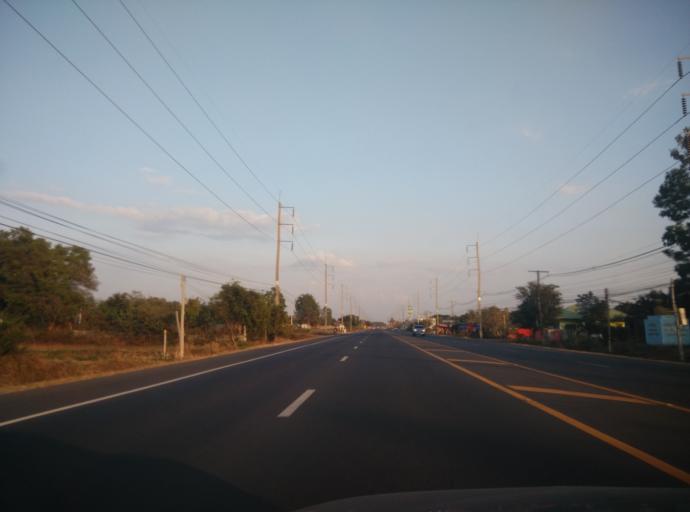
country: TH
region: Sisaket
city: Uthumphon Phisai
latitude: 15.1558
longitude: 104.1882
